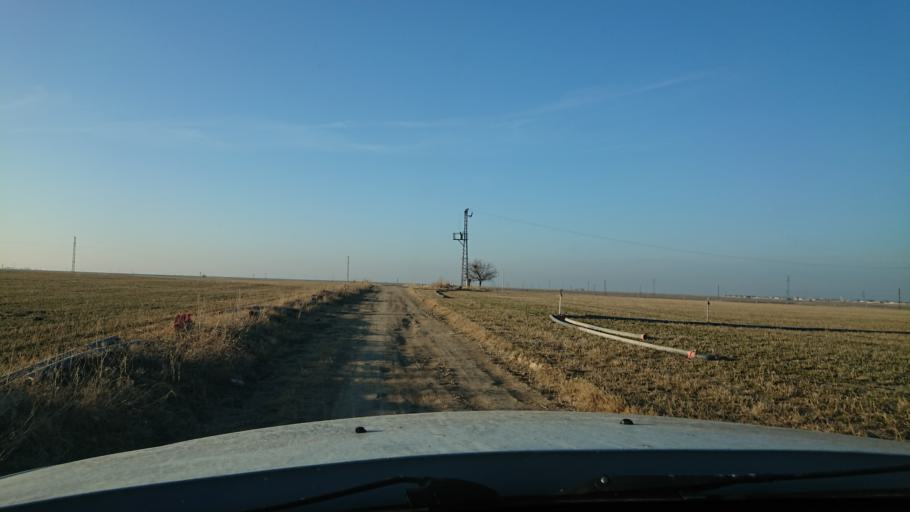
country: TR
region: Aksaray
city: Sultanhani
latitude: 38.2683
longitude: 33.5193
